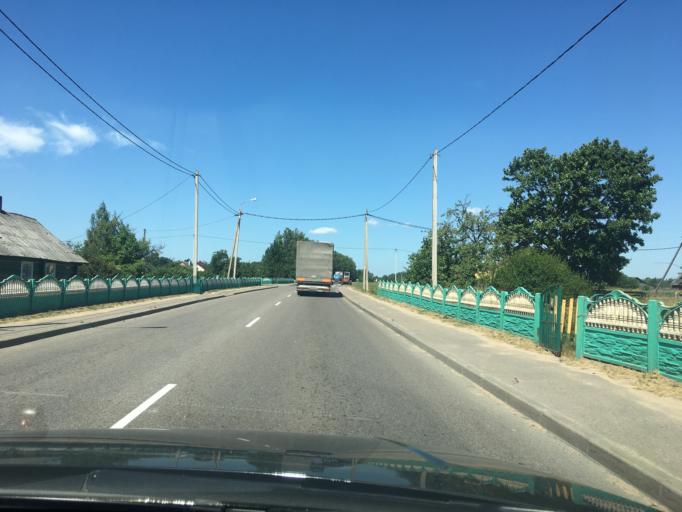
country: BY
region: Grodnenskaya
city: Iwye
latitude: 54.0352
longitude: 25.9220
